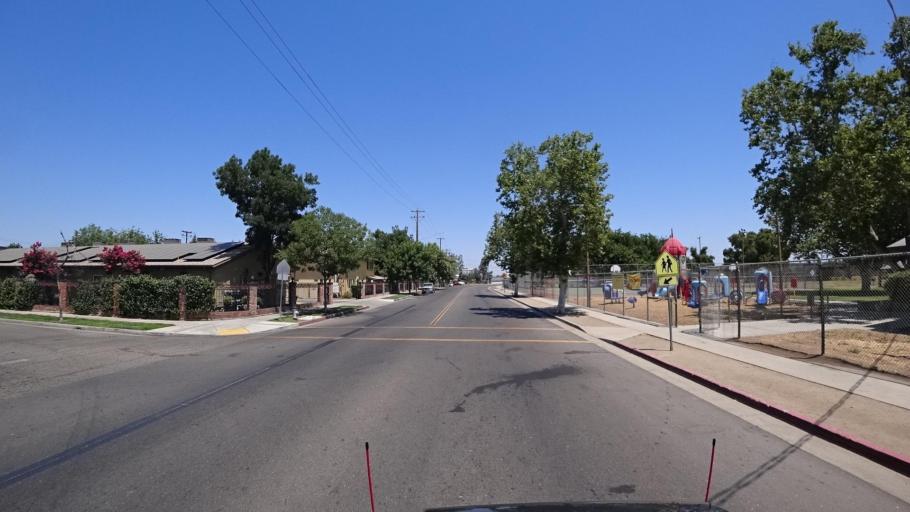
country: US
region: California
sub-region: Fresno County
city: Fresno
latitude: 36.7368
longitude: -119.8085
